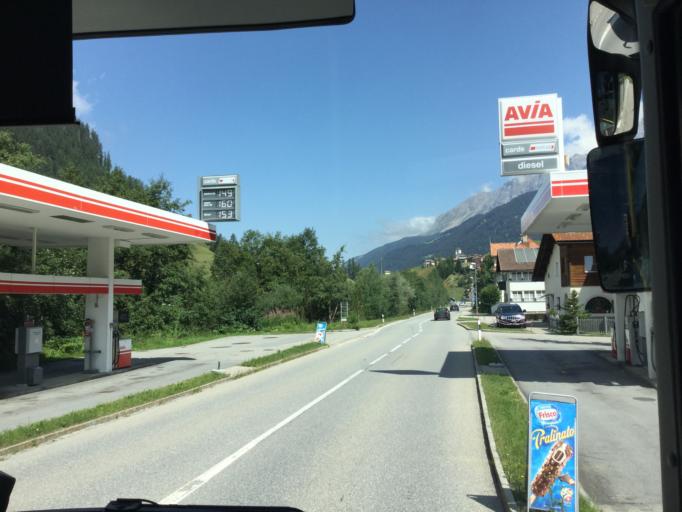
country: CH
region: Grisons
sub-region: Albula District
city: Tiefencastel
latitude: 46.5570
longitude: 9.6248
